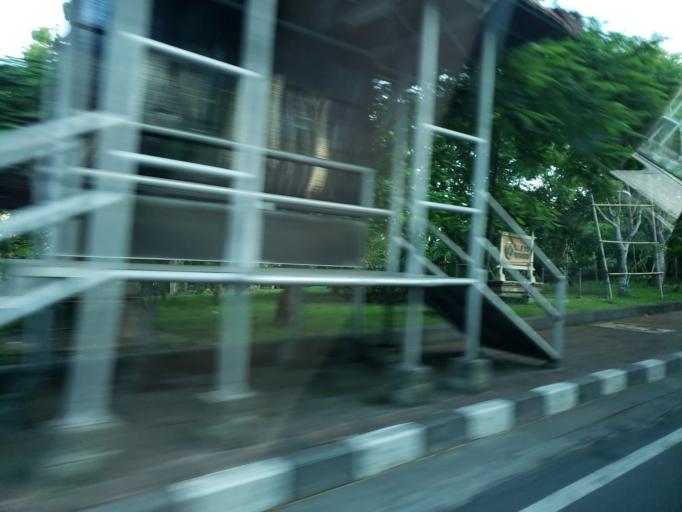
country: ID
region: Bali
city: Jimbaran
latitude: -8.7928
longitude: 115.1770
